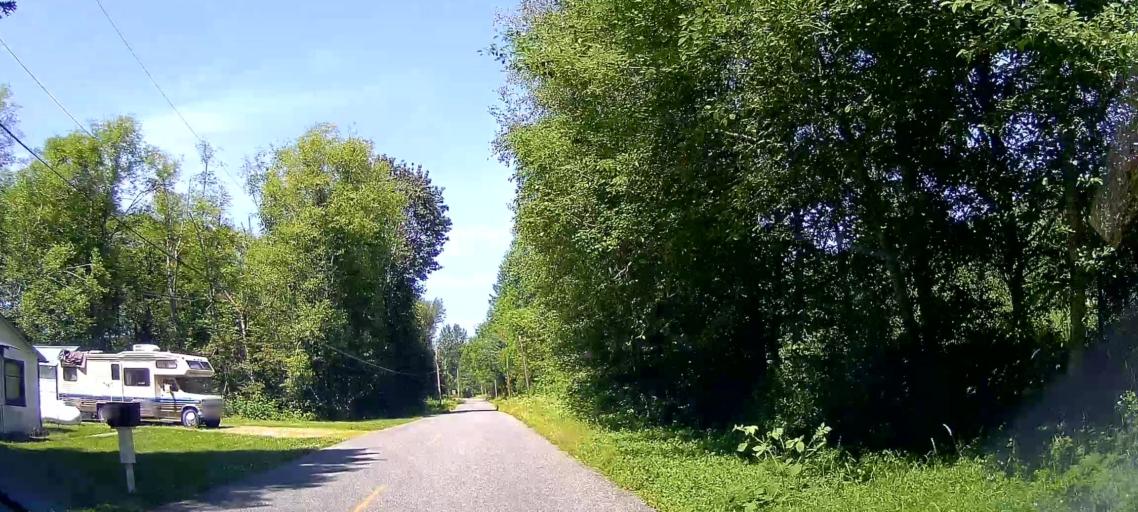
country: US
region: Washington
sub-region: Skagit County
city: Burlington
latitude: 48.5989
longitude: -122.3173
